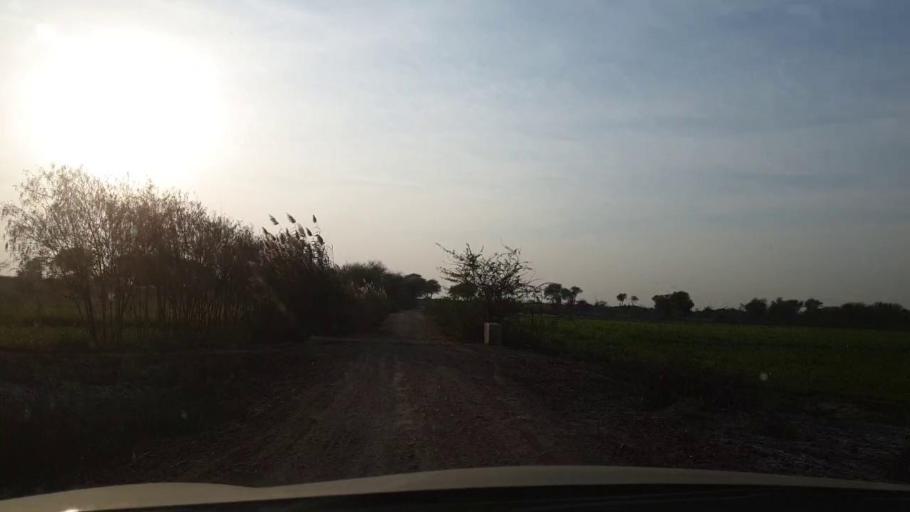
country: PK
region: Sindh
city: Tando Adam
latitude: 25.7053
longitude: 68.7387
